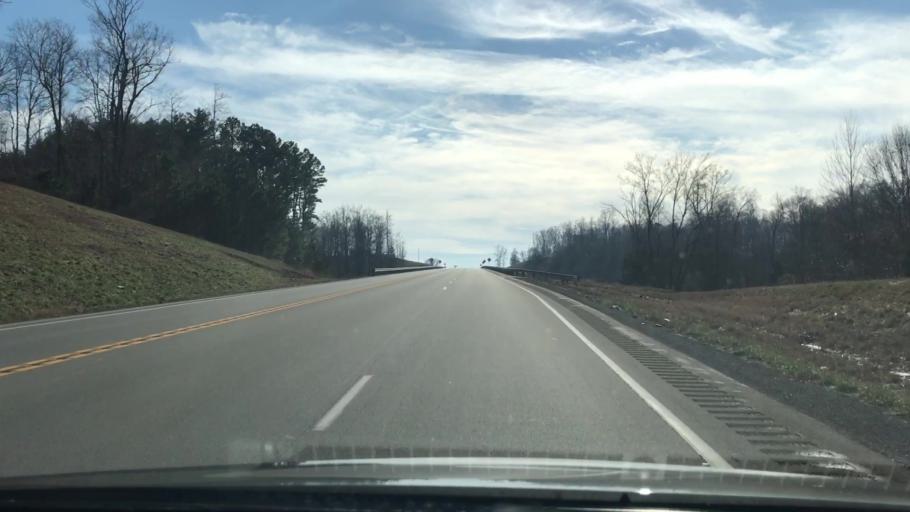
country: US
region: Kentucky
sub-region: Monroe County
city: Tompkinsville
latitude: 36.7958
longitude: -85.6872
